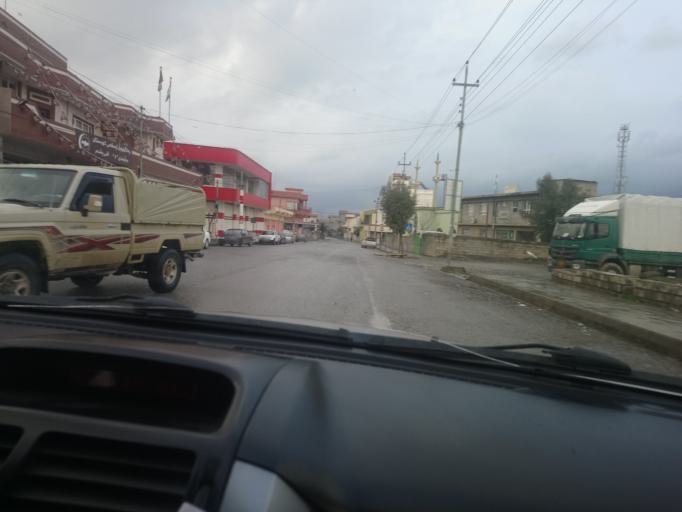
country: IQ
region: As Sulaymaniyah
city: Qeladize
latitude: 36.1822
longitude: 45.1355
